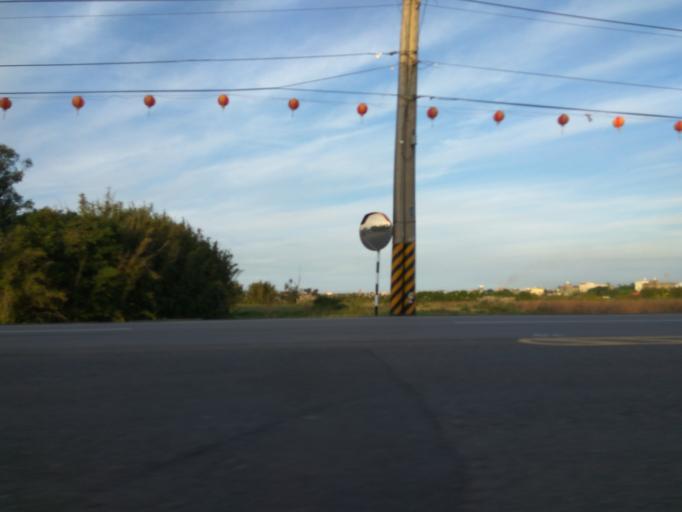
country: TW
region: Taiwan
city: Taoyuan City
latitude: 25.0075
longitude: 121.1445
